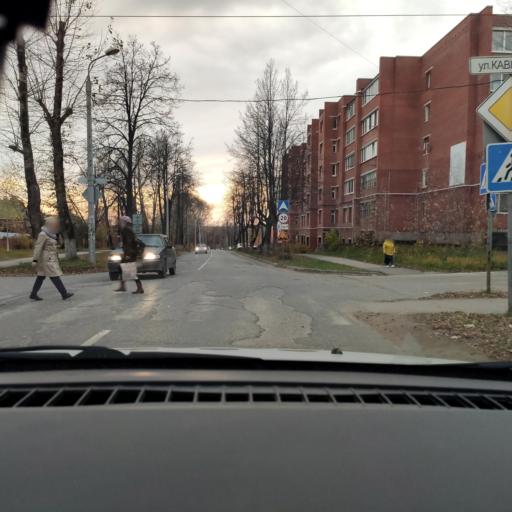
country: RU
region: Perm
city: Perm
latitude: 58.1204
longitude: 56.3821
